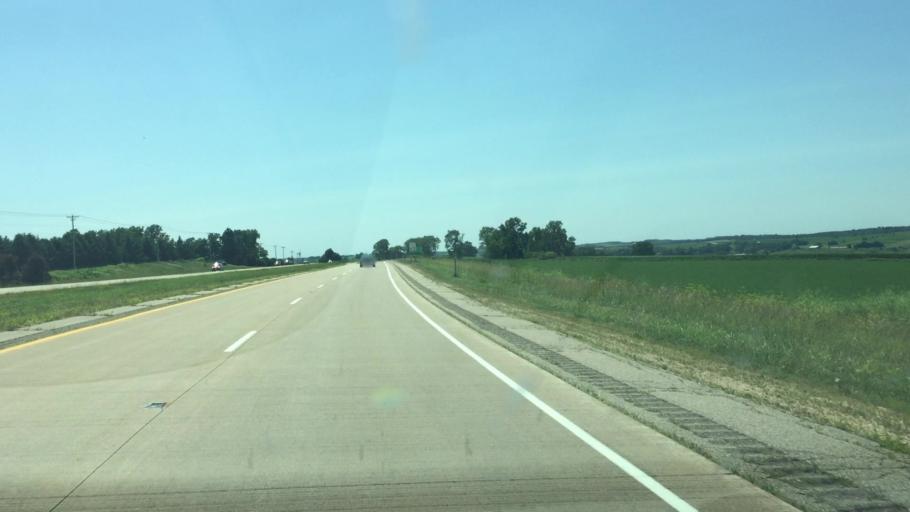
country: US
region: Wisconsin
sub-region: Iowa County
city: Mineral Point
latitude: 42.8413
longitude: -90.2070
